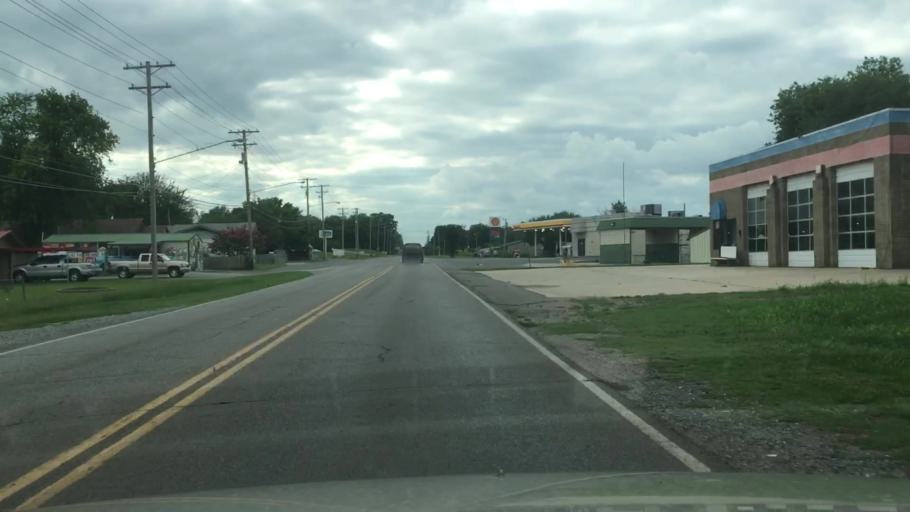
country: US
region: Oklahoma
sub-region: Cherokee County
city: Tahlequah
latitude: 35.9145
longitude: -94.9826
